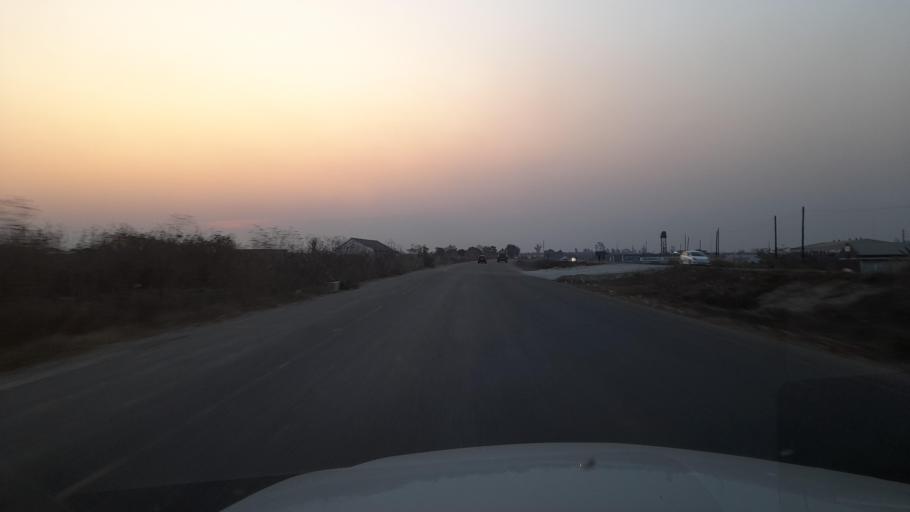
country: ZM
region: Copperbelt
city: Kitwe
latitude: -12.7633
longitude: 28.1700
